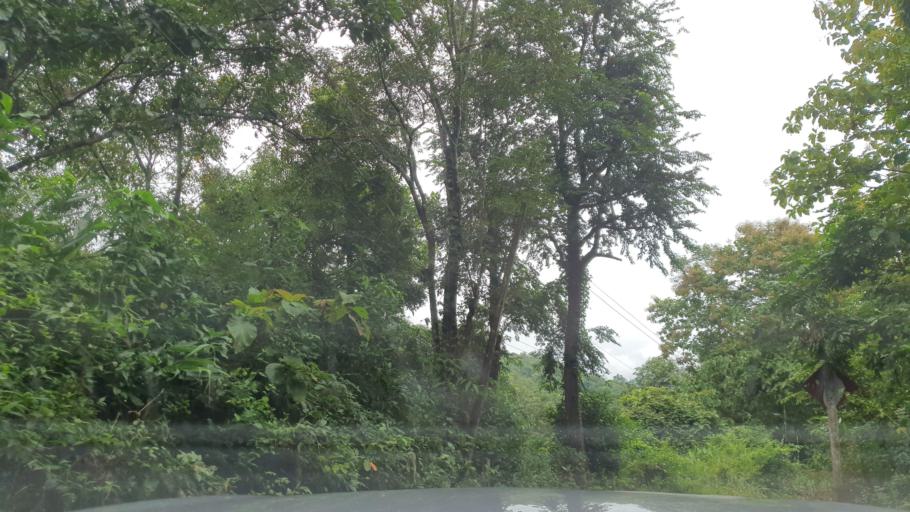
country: TH
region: Chiang Mai
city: Mae Taeng
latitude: 19.2008
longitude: 98.9362
